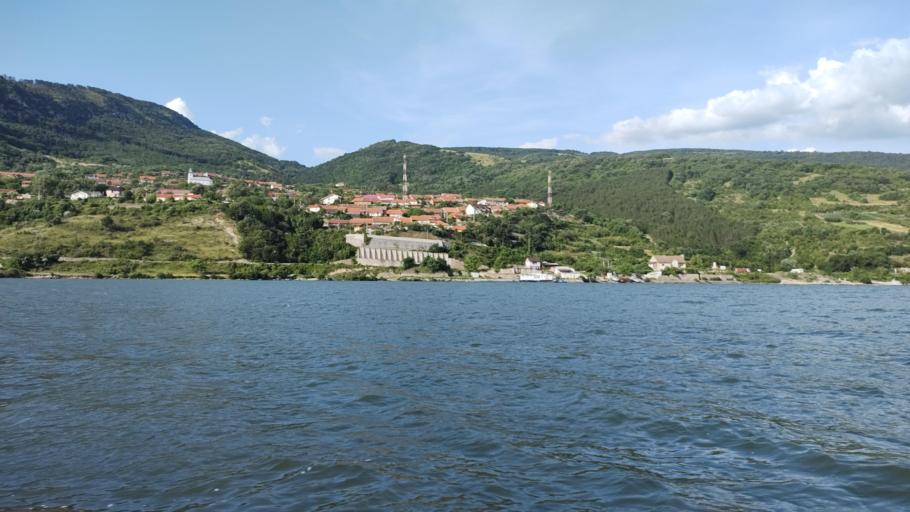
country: RO
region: Mehedinti
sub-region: Comuna Svinita
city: Svinita
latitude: 44.4932
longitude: 22.1011
